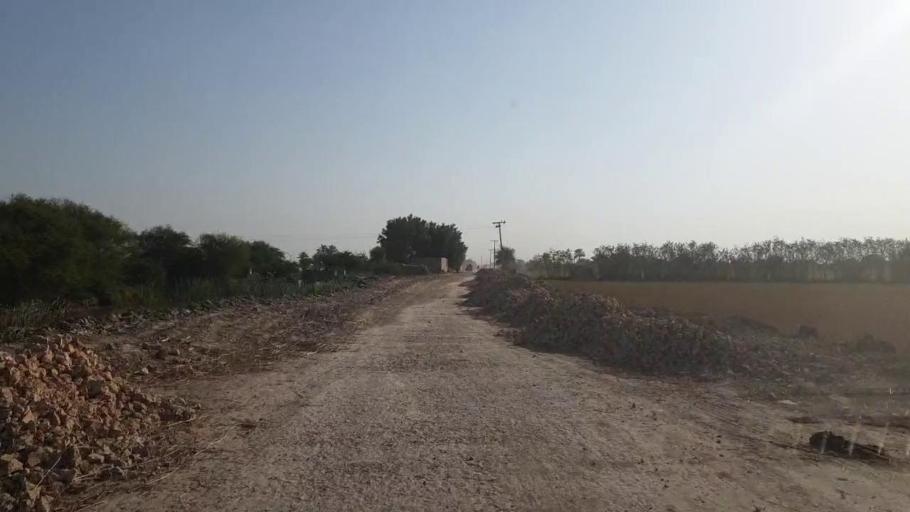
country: PK
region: Sindh
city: Talhar
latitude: 24.9253
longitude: 68.7476
